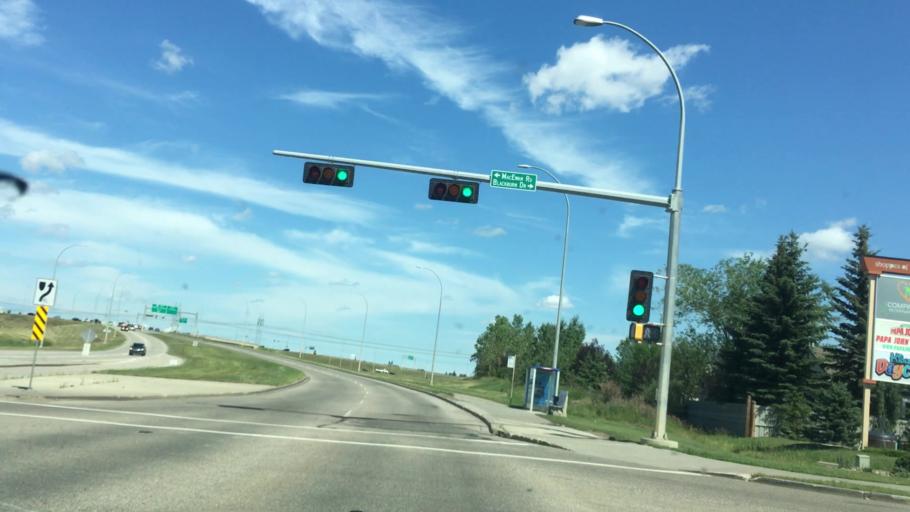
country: CA
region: Alberta
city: Beaumont
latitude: 53.4294
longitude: -113.5164
